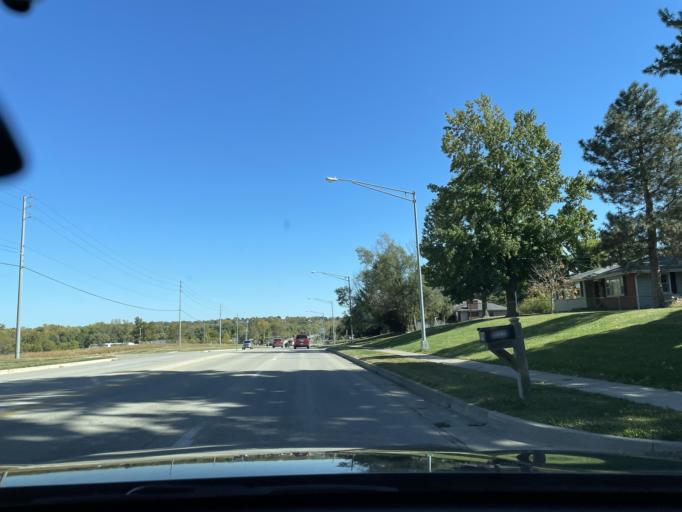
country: US
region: Missouri
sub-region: Andrew County
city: Country Club Village
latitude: 39.7815
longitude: -94.7711
